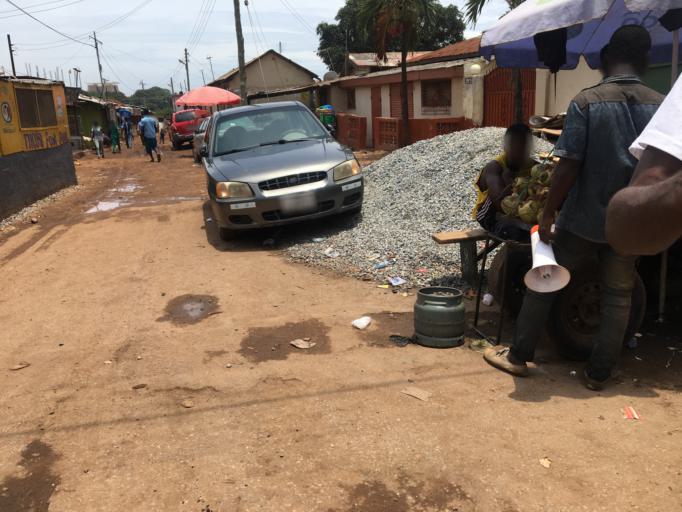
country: GH
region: Greater Accra
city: Accra
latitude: 5.5817
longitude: -0.1972
